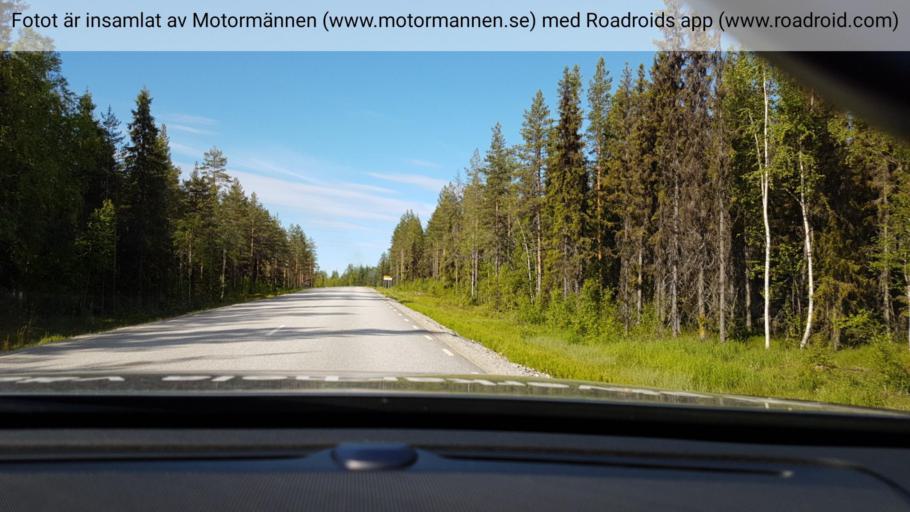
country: SE
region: Vaesterbotten
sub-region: Bjurholms Kommun
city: Bjurholm
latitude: 64.1556
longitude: 19.3580
